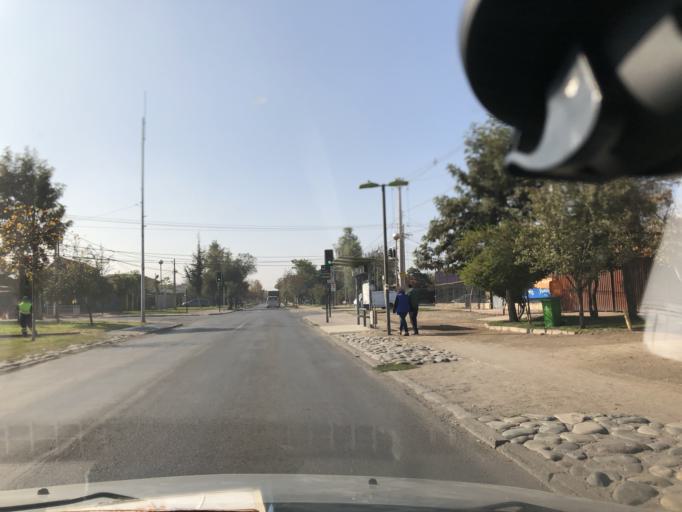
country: CL
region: Santiago Metropolitan
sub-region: Provincia de Cordillera
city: Puente Alto
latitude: -33.6181
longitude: -70.5863
